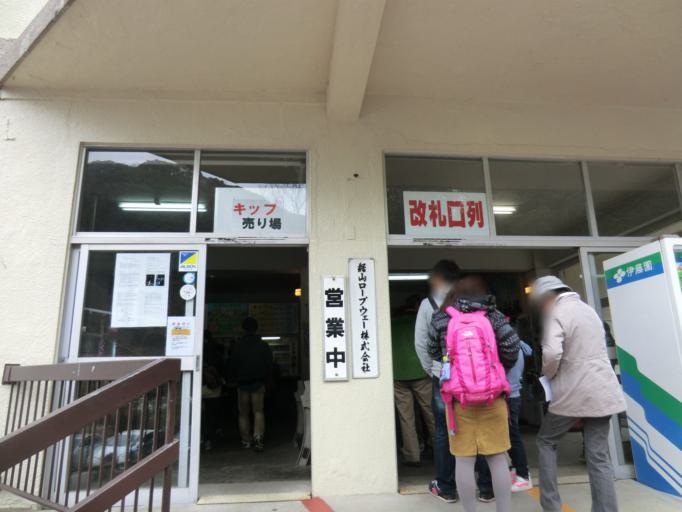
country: JP
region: Chiba
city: Futtsu
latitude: 35.1621
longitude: 139.8231
